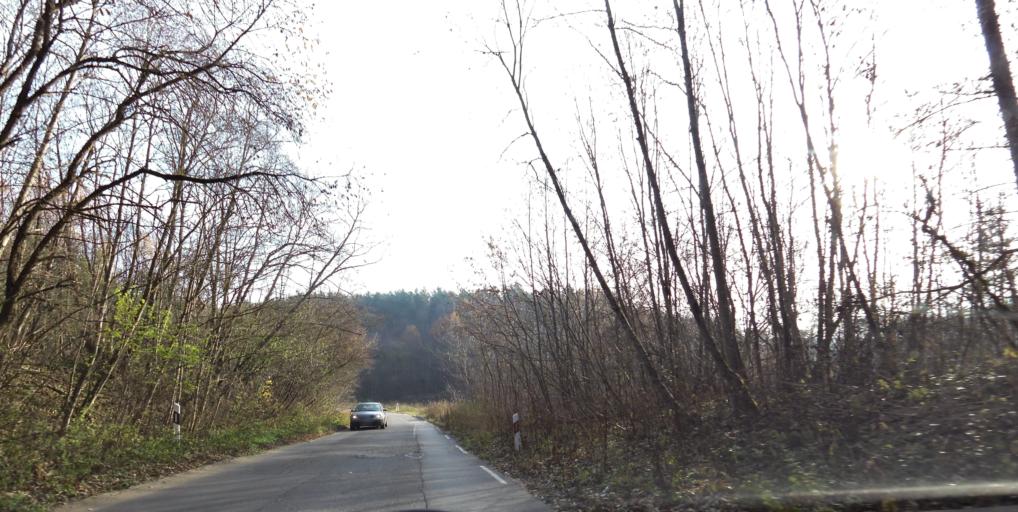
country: LT
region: Vilnius County
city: Pilaite
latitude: 54.6970
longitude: 25.1865
